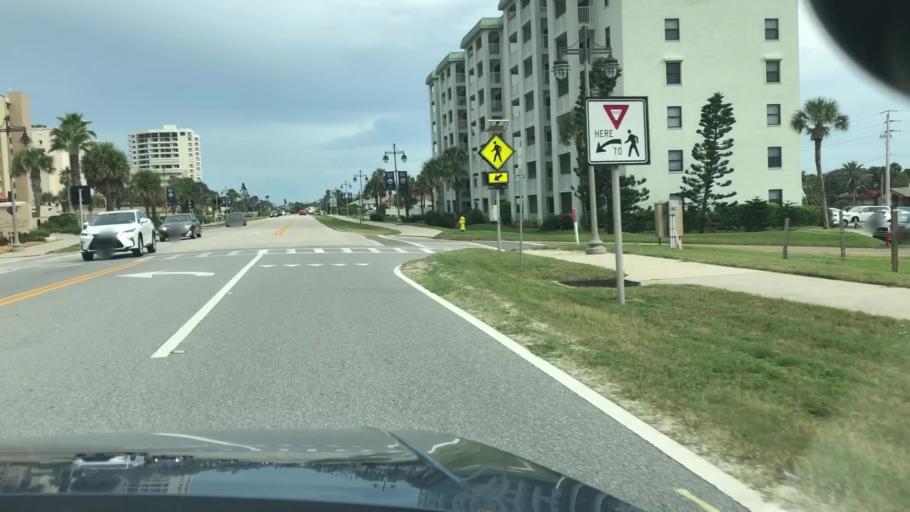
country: US
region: Florida
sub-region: Volusia County
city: Port Orange
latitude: 29.1414
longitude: -80.9639
